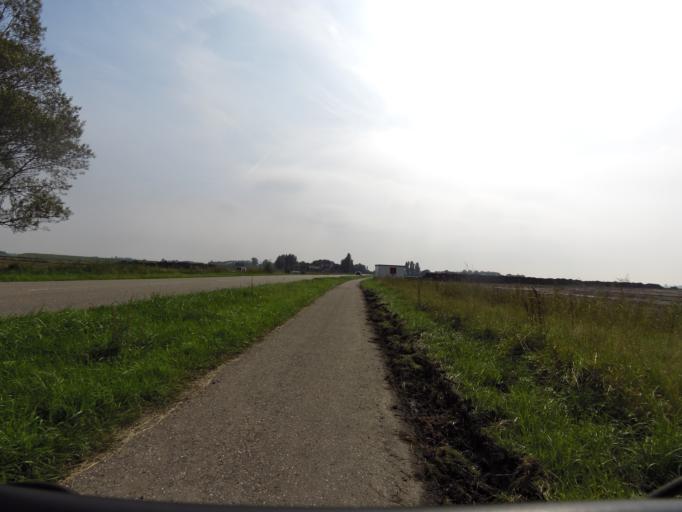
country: NL
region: Zeeland
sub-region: Gemeente Middelburg
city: Middelburg
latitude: 51.5388
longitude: 3.6025
